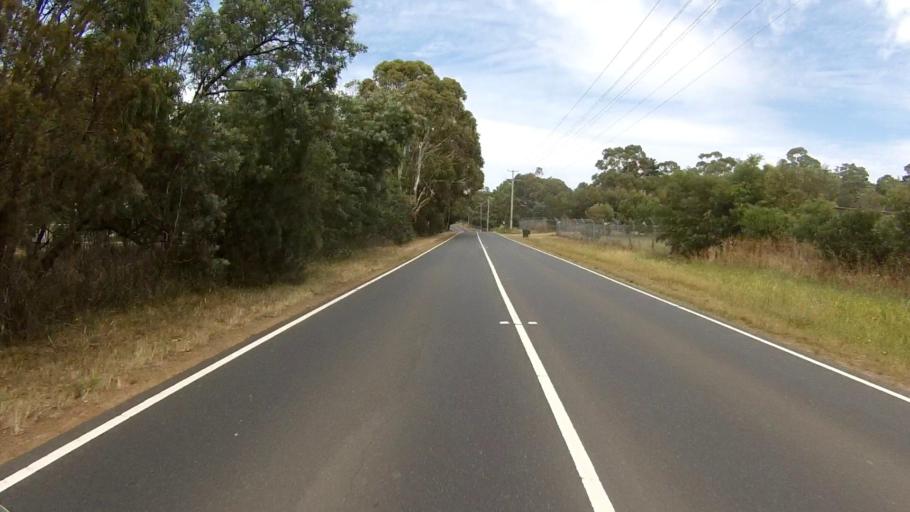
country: AU
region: Tasmania
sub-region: Clarence
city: Acton Park
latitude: -42.8767
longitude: 147.4826
